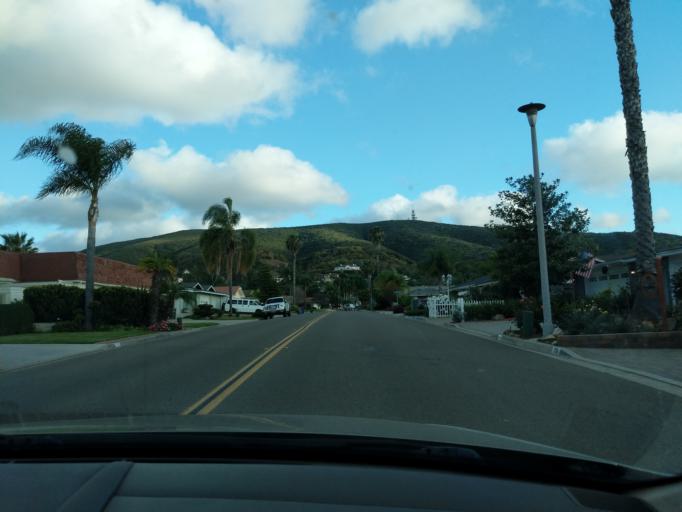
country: US
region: California
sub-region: San Diego County
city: Lake San Marcos
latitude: 33.1231
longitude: -117.2034
